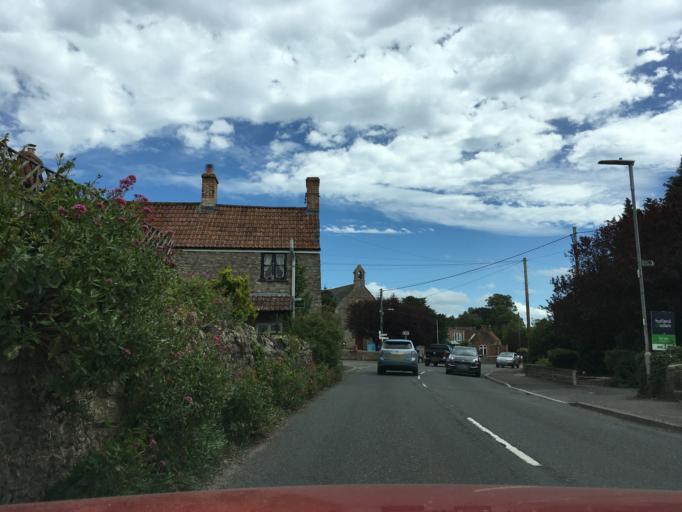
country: GB
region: England
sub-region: Somerset
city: Wells
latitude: 51.2262
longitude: -2.6993
